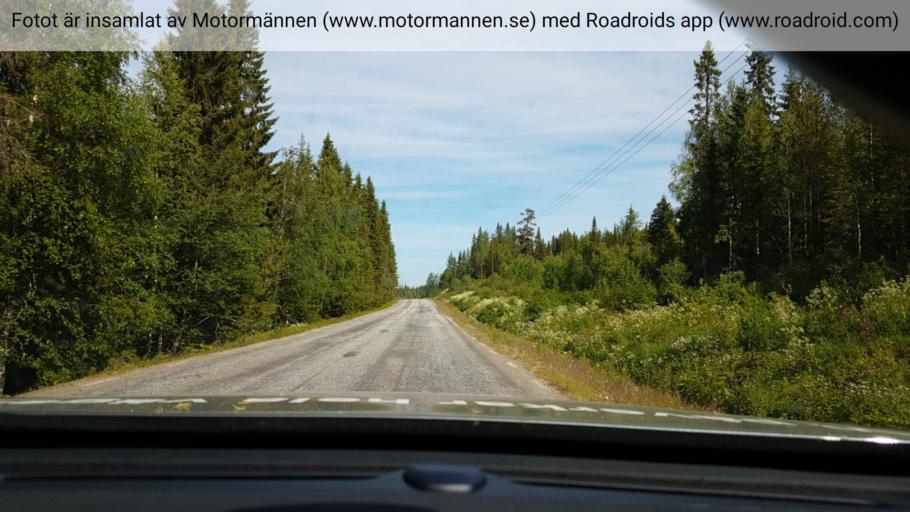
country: SE
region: Vaesterbotten
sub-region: Vilhelmina Kommun
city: Sjoberg
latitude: 64.5394
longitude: 15.8870
